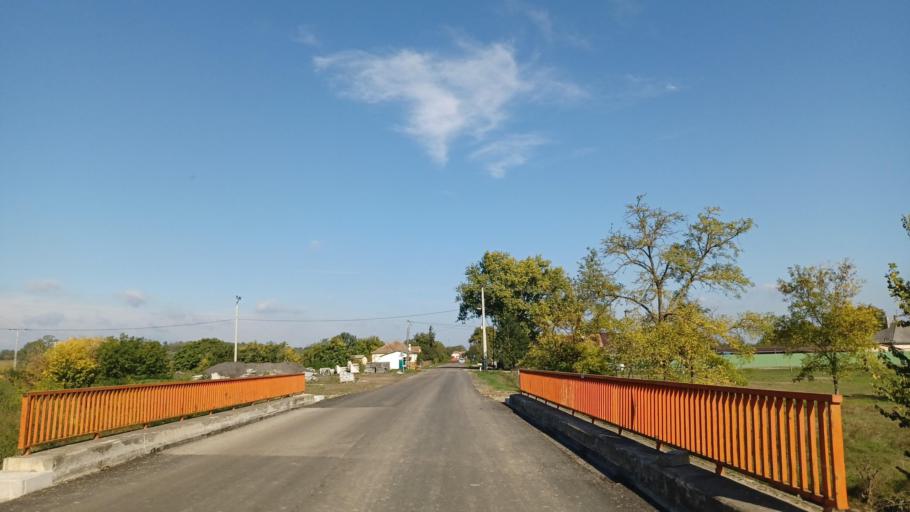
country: HU
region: Tolna
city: Nagydorog
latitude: 46.5996
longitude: 18.5938
